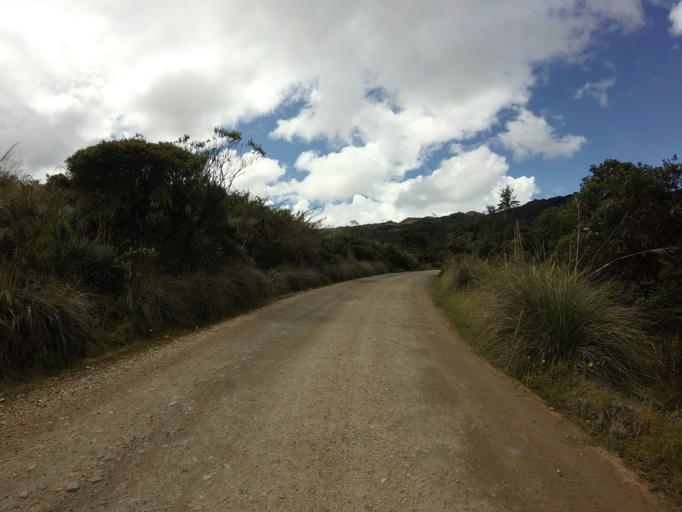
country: CO
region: Cundinamarca
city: Junin
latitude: 4.6260
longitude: -73.7229
